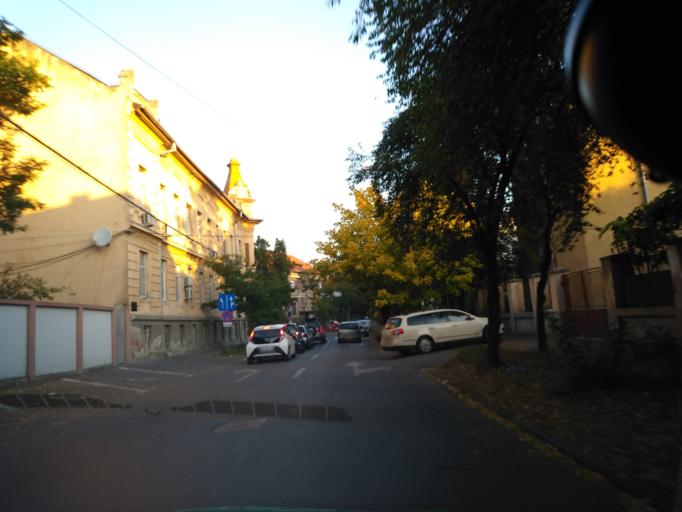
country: RO
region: Timis
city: Timisoara
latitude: 45.7441
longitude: 21.2302
